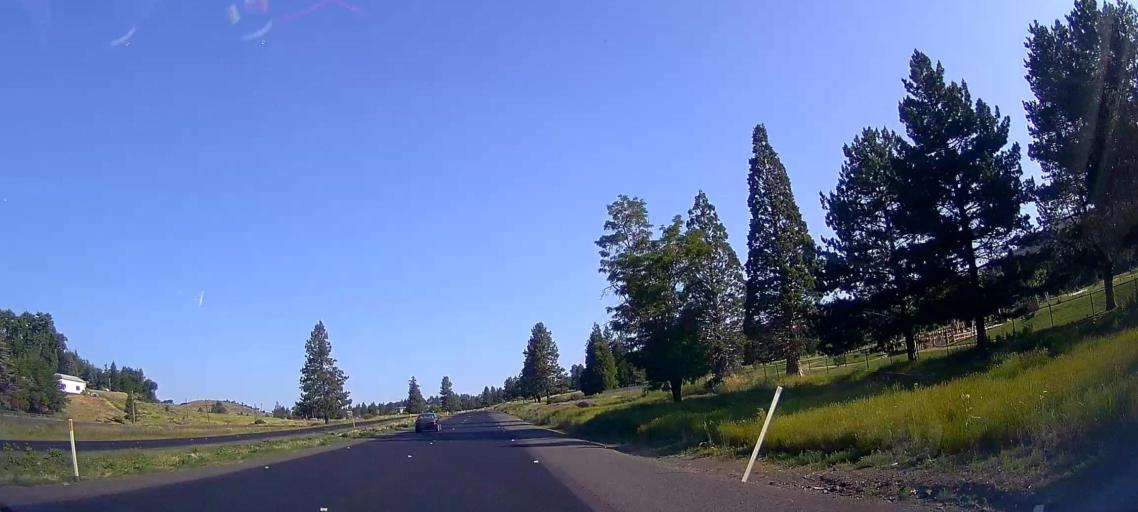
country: US
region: Oregon
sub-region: Klamath County
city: Klamath Falls
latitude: 42.2380
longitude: -121.7792
